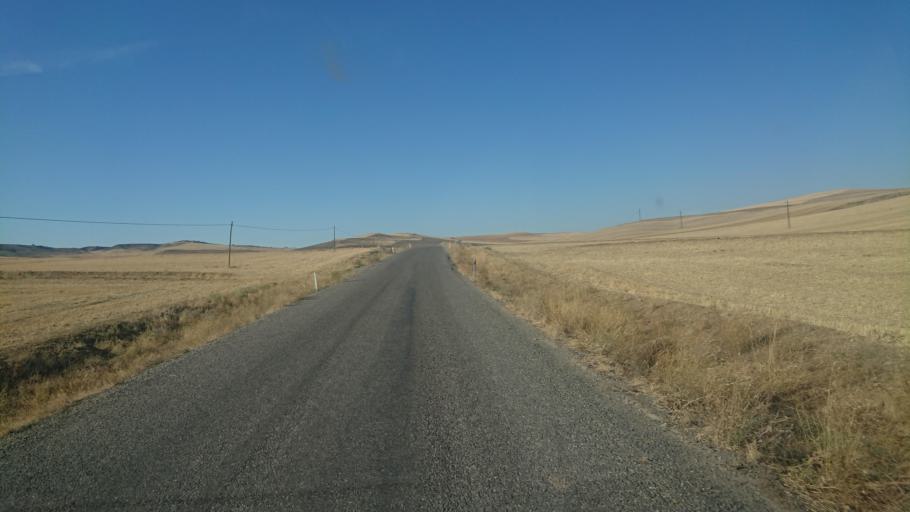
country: TR
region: Aksaray
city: Agacoren
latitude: 38.7921
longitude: 33.7126
